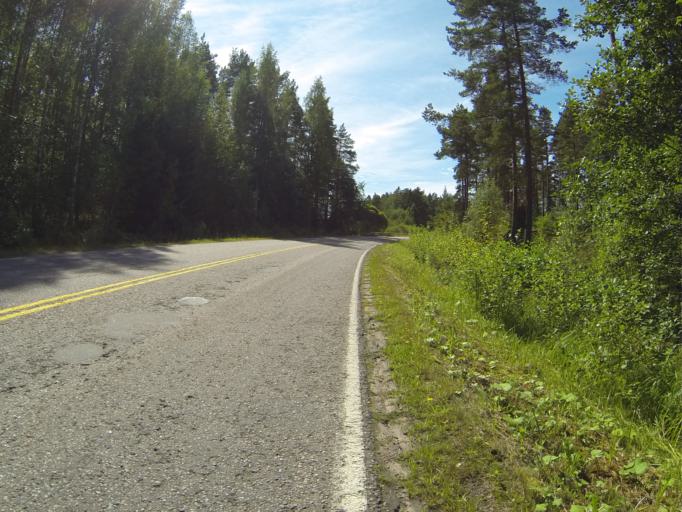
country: FI
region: Varsinais-Suomi
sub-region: Salo
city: Saerkisalo
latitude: 60.2712
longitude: 22.9829
